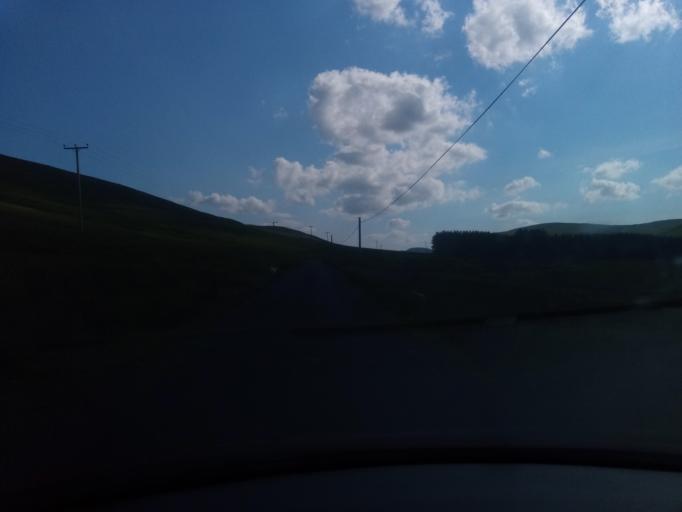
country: GB
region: Scotland
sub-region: The Scottish Borders
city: Innerleithen
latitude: 55.5022
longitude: -3.1133
